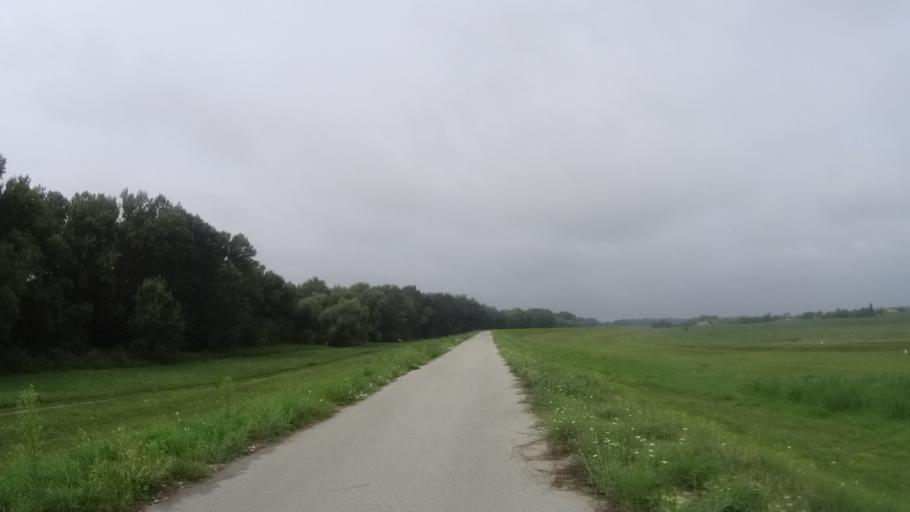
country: SK
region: Nitriansky
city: Komarno
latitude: 47.7430
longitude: 18.1907
